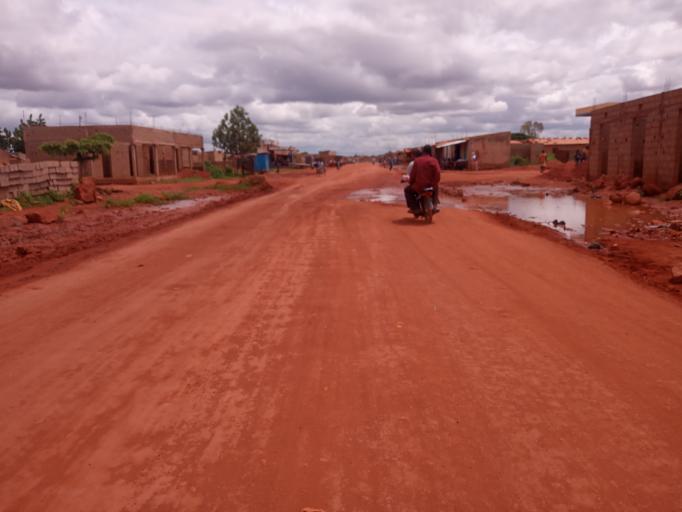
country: ML
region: Bamako
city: Bamako
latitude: 12.5341
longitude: -7.9944
